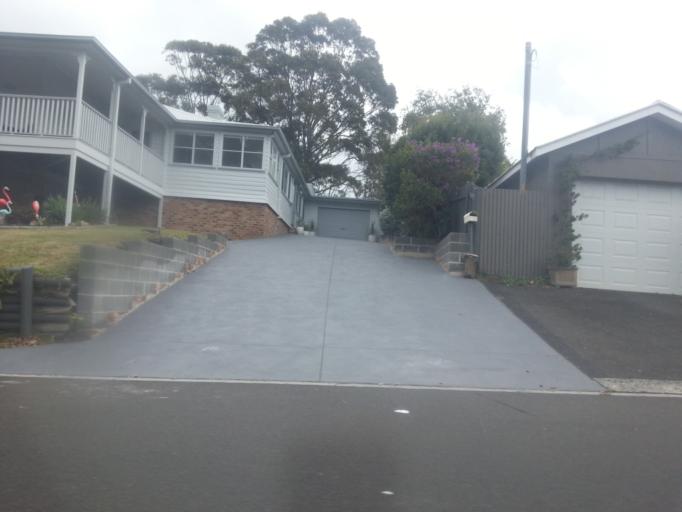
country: AU
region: New South Wales
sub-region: Wollongong
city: Bulli
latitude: -34.3143
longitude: 150.9176
